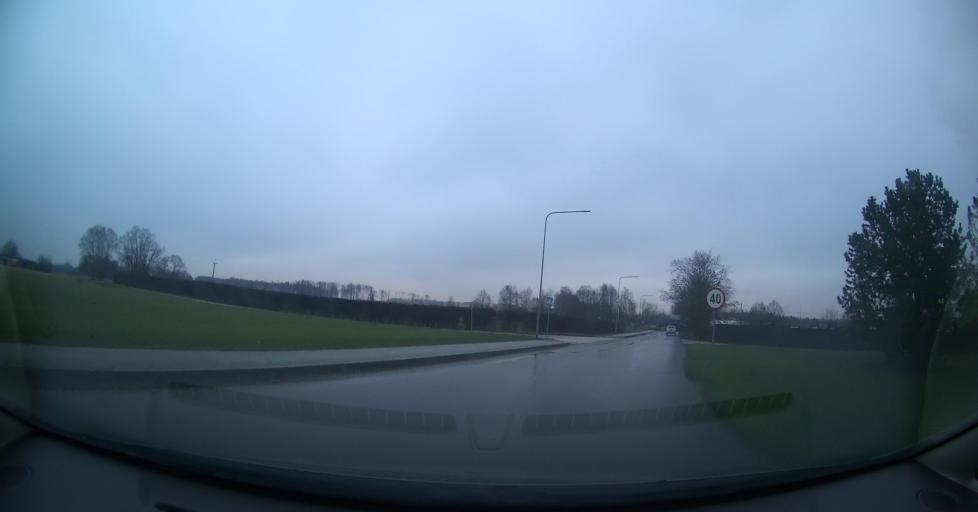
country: EE
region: Tartu
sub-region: Tartu linn
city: Tartu
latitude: 58.3704
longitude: 26.7950
